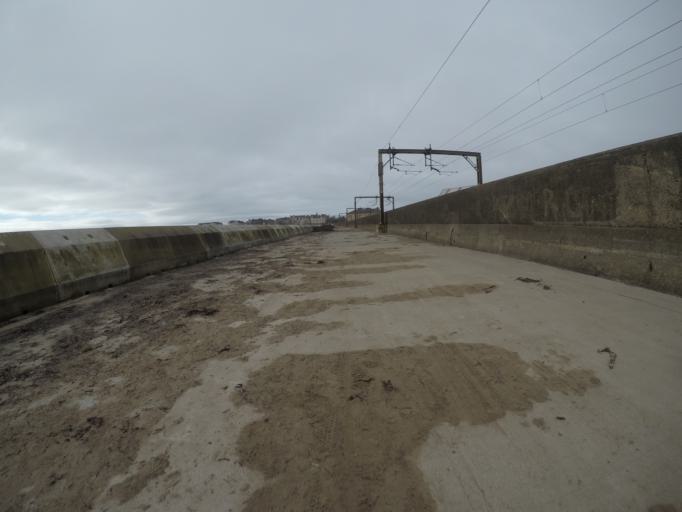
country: GB
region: Scotland
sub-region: North Ayrshire
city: Saltcoats
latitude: 55.6332
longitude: -4.7770
